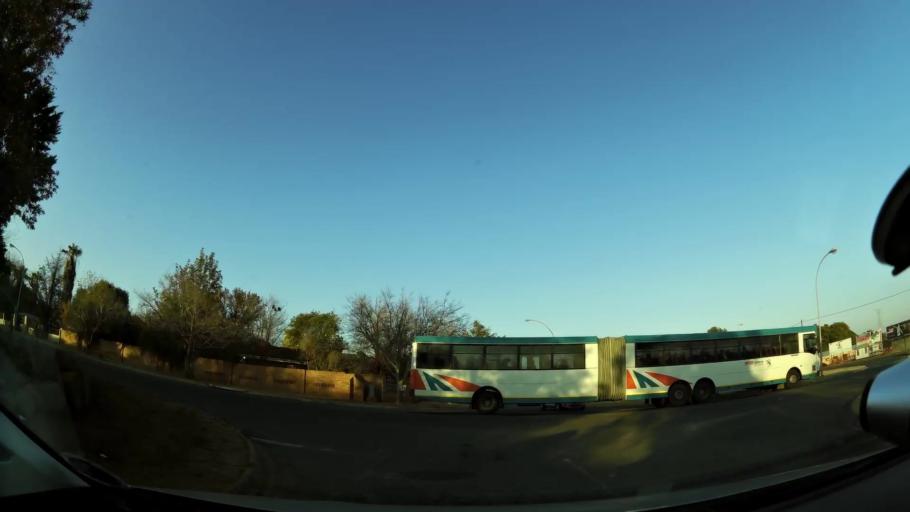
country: ZA
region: Orange Free State
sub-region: Mangaung Metropolitan Municipality
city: Bloemfontein
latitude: -29.0872
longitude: 26.1549
